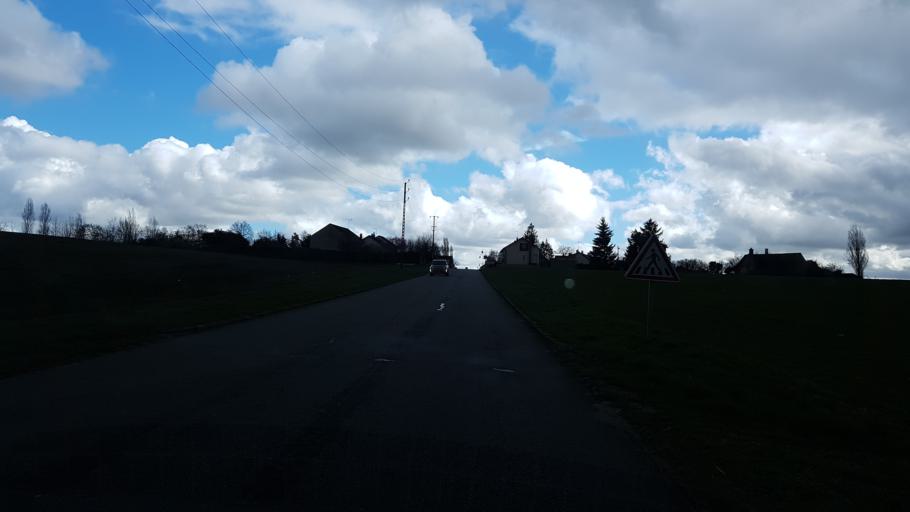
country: FR
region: Ile-de-France
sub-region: Departement des Yvelines
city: Rambouillet
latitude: 48.6181
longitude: 1.8357
